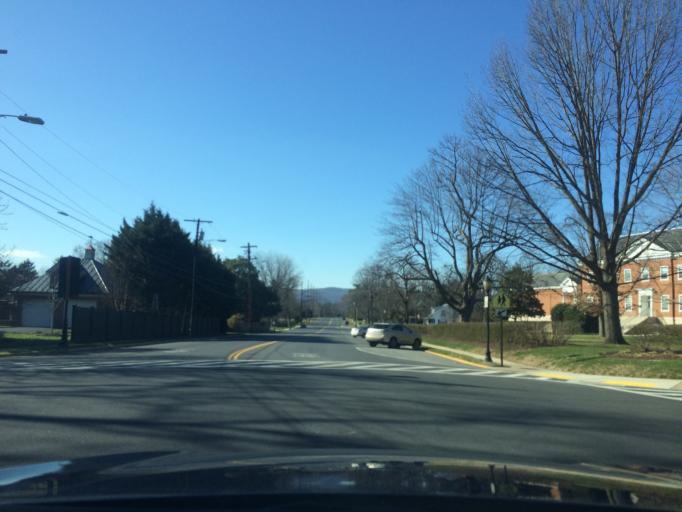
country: US
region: Maryland
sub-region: Frederick County
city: Frederick
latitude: 39.4200
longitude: -77.4198
